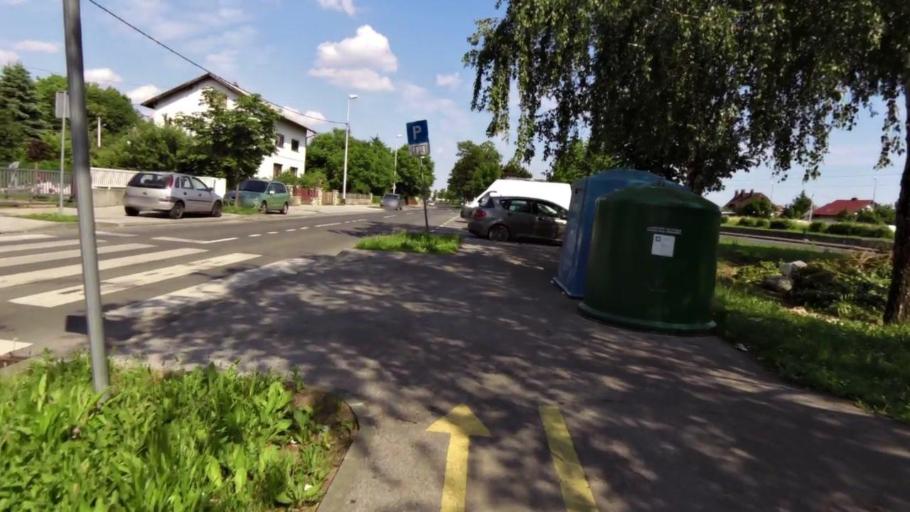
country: HR
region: Zagrebacka
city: Bestovje
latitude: 45.8157
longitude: 15.8426
